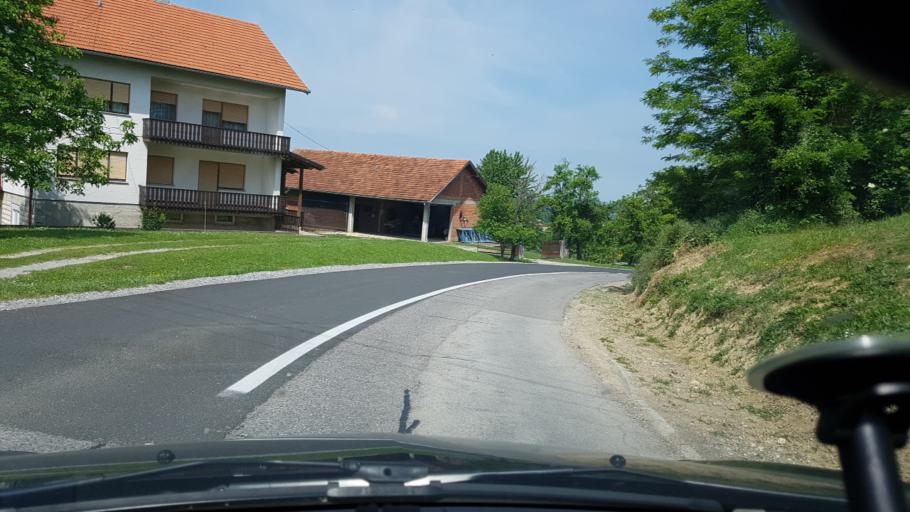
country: HR
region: Krapinsko-Zagorska
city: Marija Bistrica
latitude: 46.0053
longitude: 16.0889
